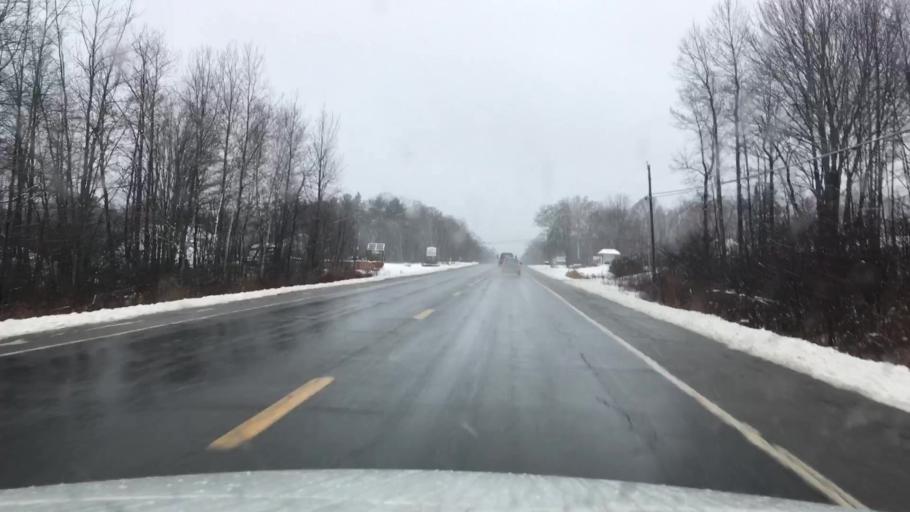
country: US
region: Maine
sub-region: Knox County
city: Warren
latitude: 44.1466
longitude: -69.1974
